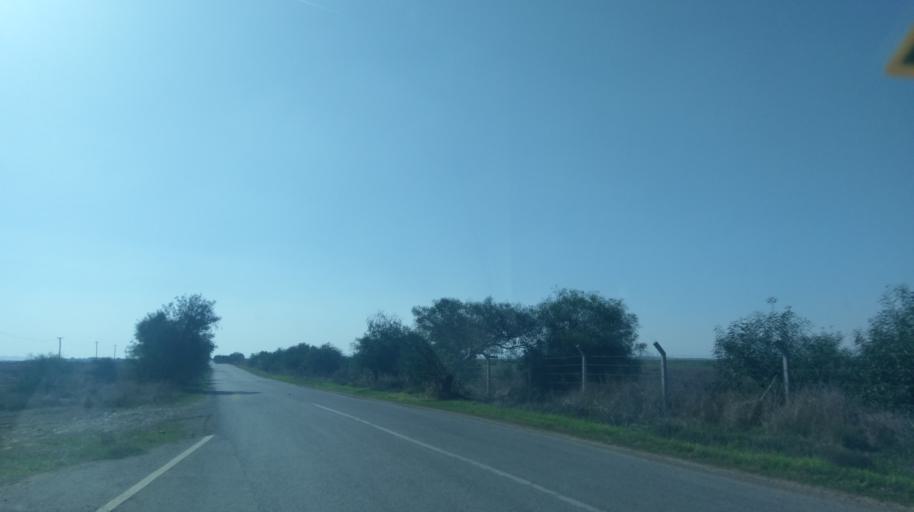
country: CY
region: Larnaka
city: Athienou
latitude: 35.1242
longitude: 33.5065
